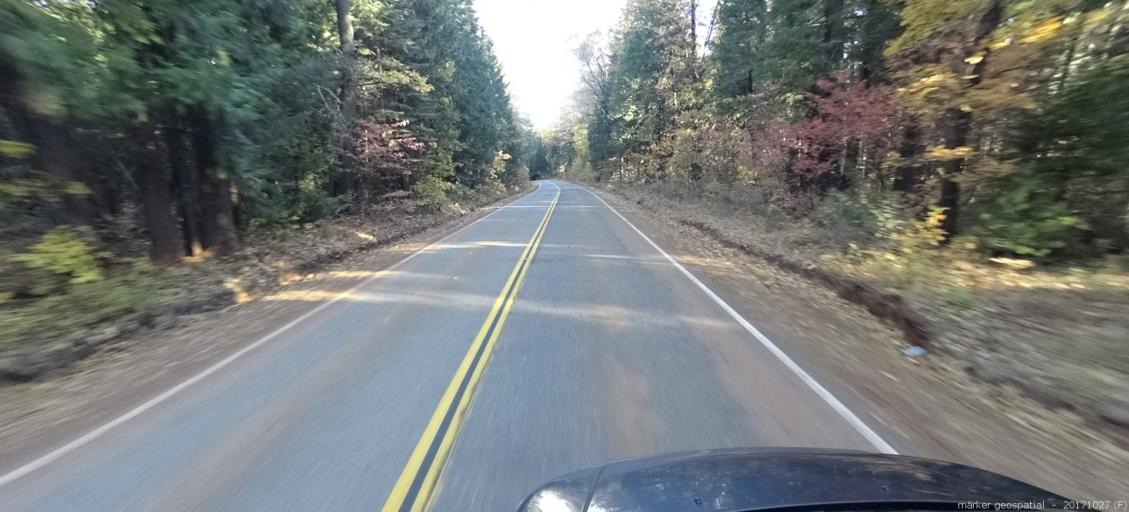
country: US
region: California
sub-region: Shasta County
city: Burney
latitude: 40.9751
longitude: -121.9306
